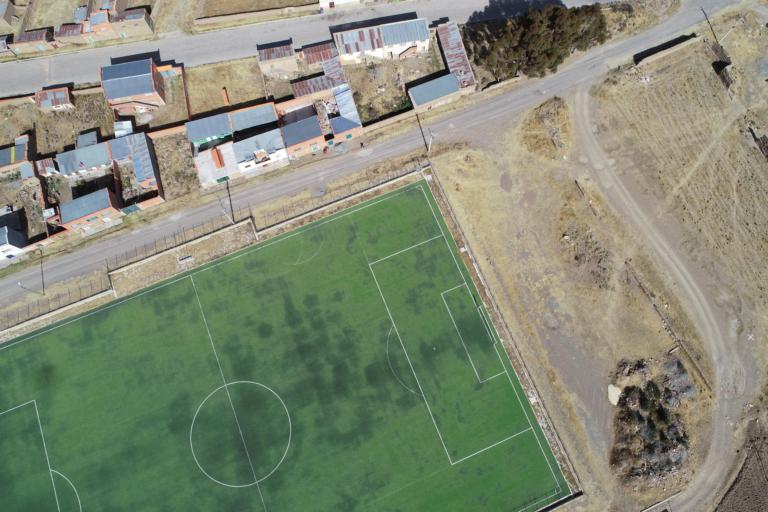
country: BO
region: La Paz
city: Achacachi
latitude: -15.8953
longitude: -68.9082
